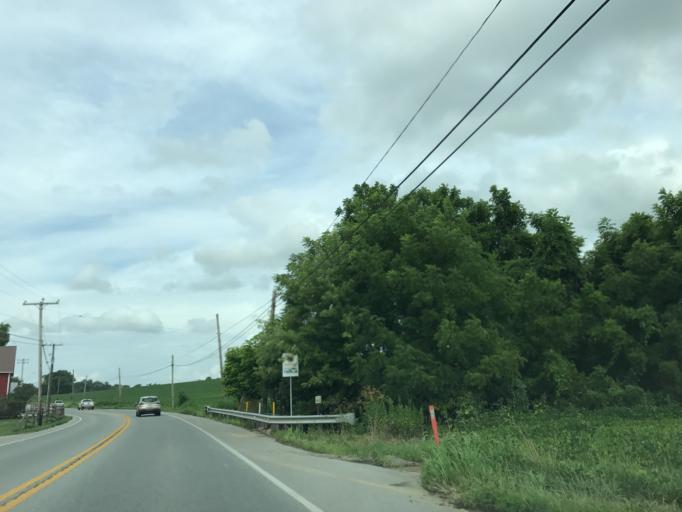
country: US
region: Pennsylvania
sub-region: York County
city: Spring Grove
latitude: 39.8343
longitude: -76.9158
